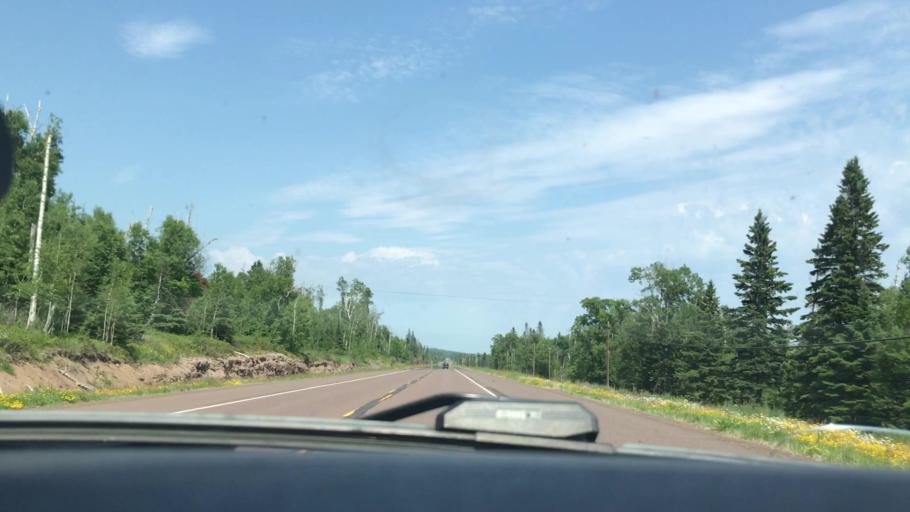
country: US
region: Minnesota
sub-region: Cook County
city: Grand Marais
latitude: 47.6212
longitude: -90.7475
